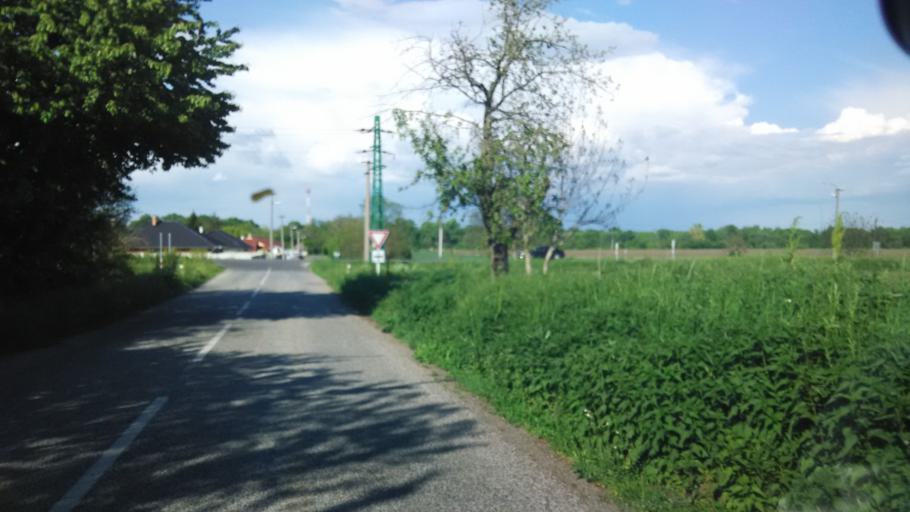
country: SK
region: Nitriansky
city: Levice
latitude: 48.1624
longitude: 18.5518
